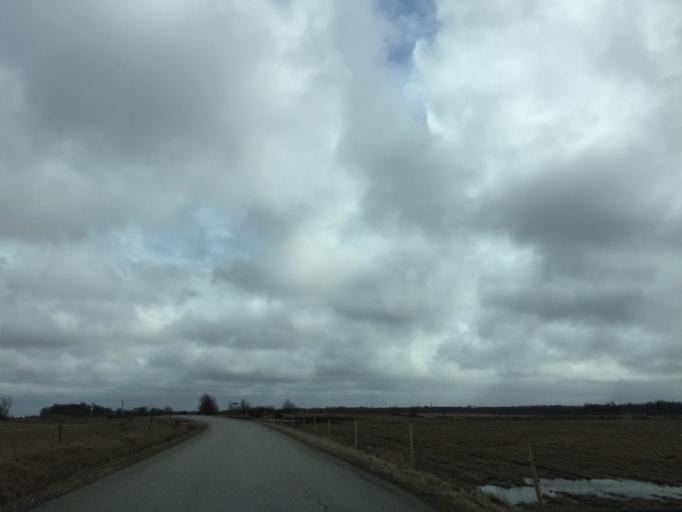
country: EE
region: Laeaene
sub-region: Lihula vald
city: Lihula
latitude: 58.7288
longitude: 23.8851
